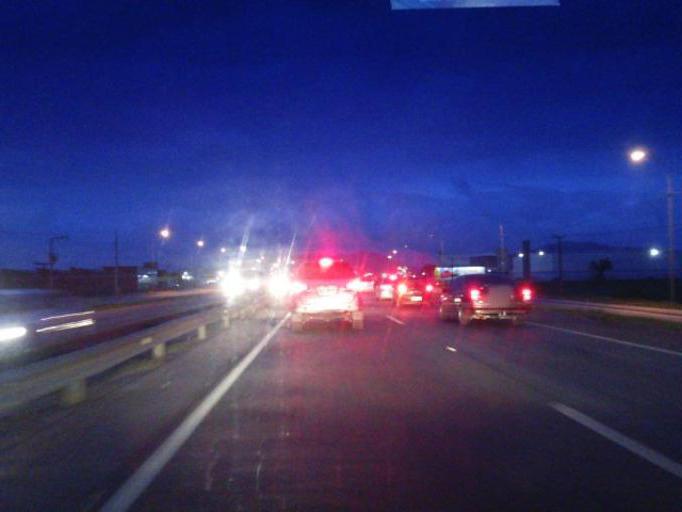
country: BR
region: Santa Catarina
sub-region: Itajai
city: Itajai
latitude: -26.8580
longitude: -48.7276
